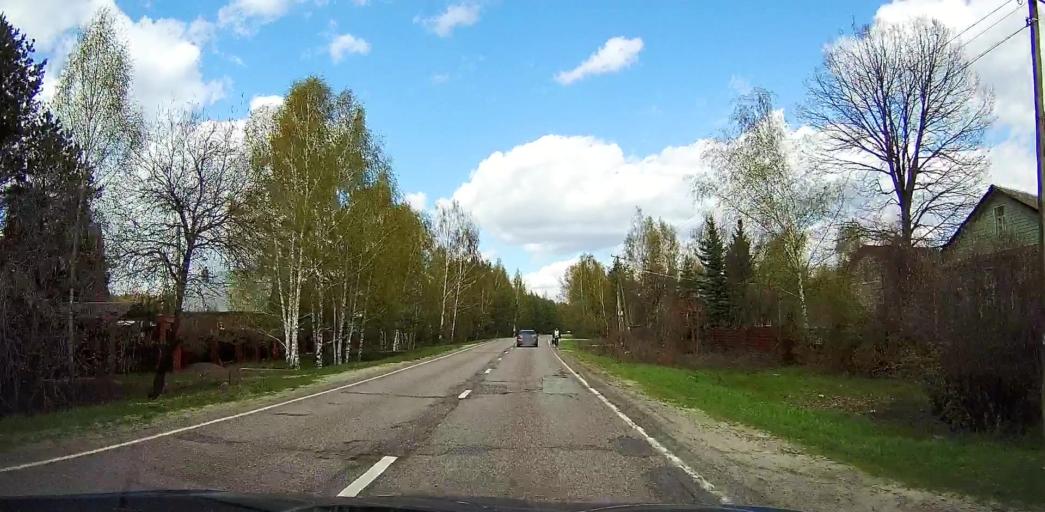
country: RU
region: Moskovskaya
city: Davydovo
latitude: 55.5892
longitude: 38.8311
